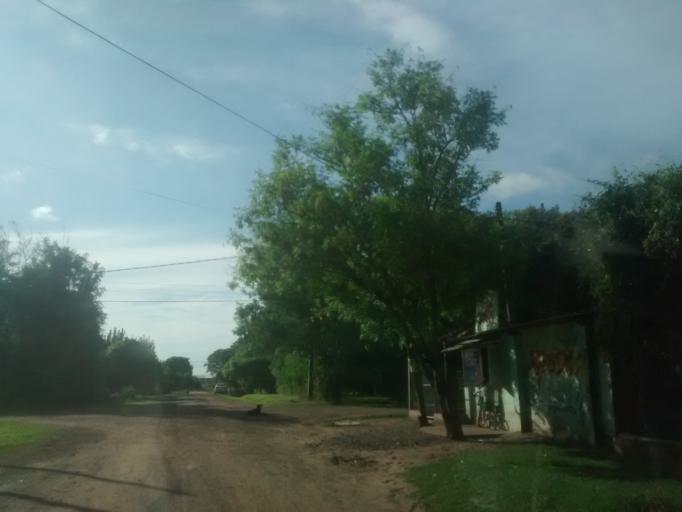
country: AR
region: Chaco
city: Puerto Tirol
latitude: -27.3760
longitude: -59.0975
